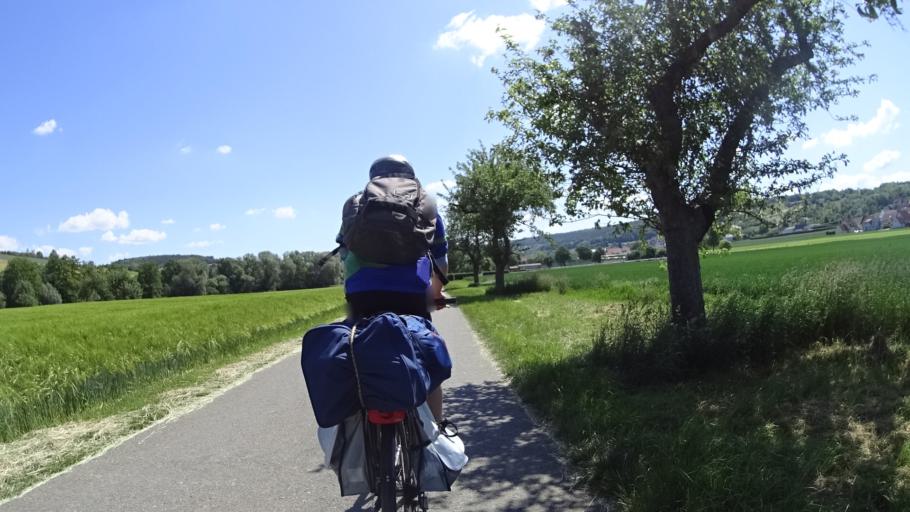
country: DE
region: Bavaria
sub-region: Regierungsbezirk Unterfranken
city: Tauberrettersheim
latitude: 49.4960
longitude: 9.9262
